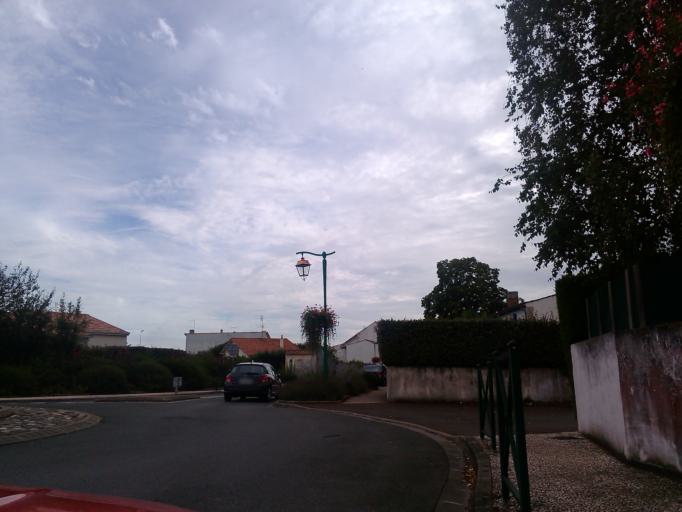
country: FR
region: Poitou-Charentes
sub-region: Departement de la Charente-Maritime
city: Breuillet
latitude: 45.6949
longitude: -1.0511
